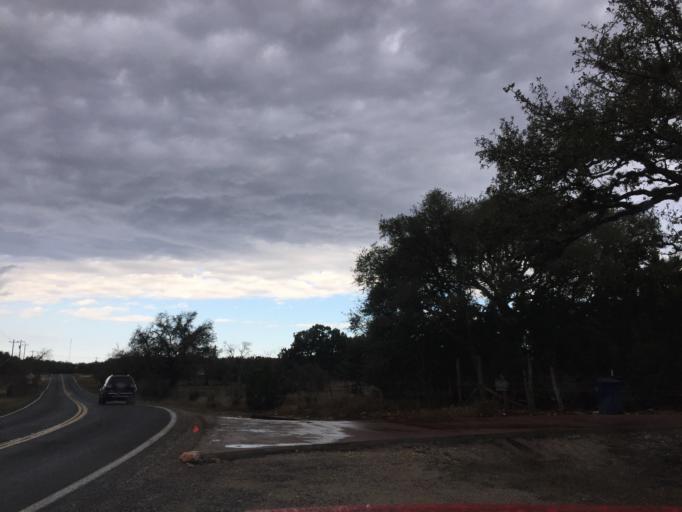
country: US
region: Texas
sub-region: Williamson County
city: Leander
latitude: 30.6086
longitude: -97.9335
